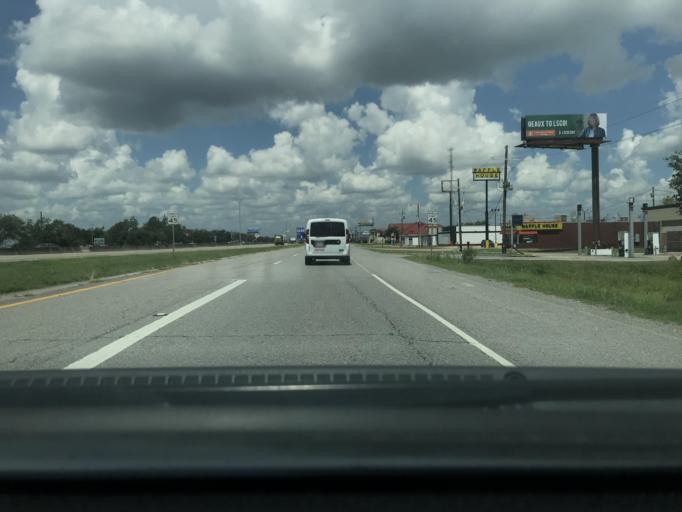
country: US
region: Louisiana
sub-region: Calcasieu Parish
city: Westlake
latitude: 30.2374
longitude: -93.2245
